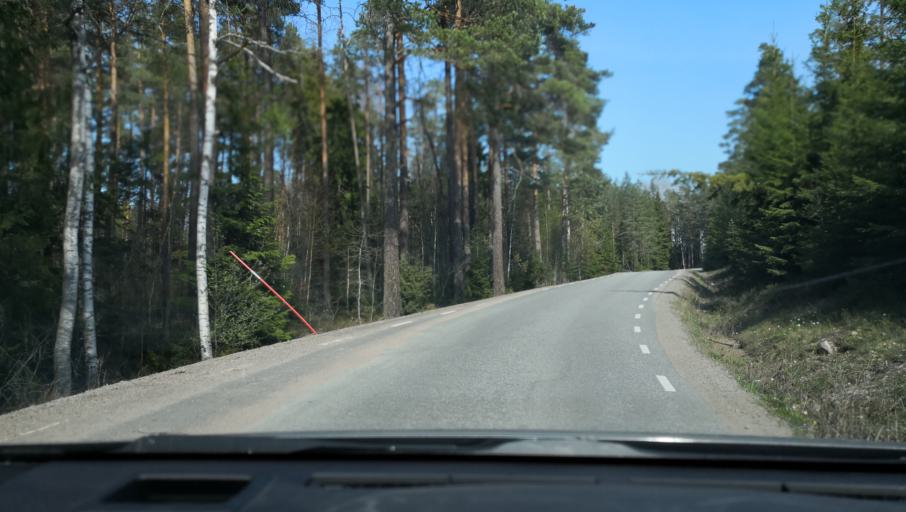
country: SE
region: Vaestmanland
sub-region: Sala Kommun
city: Sala
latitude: 60.0013
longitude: 16.6653
